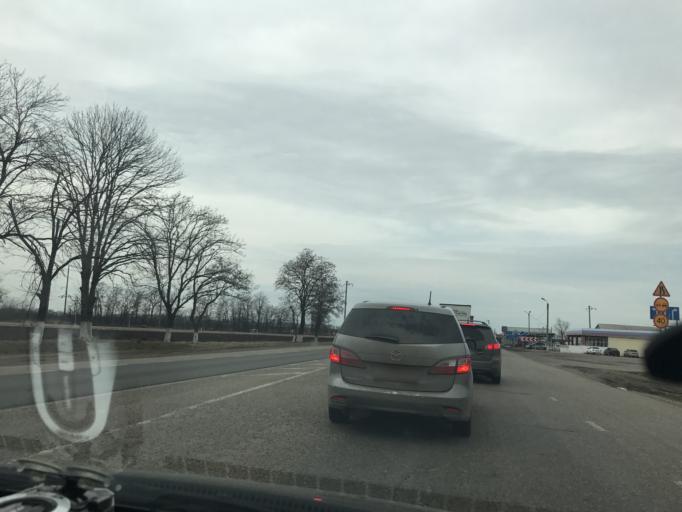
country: RU
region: Krasnodarskiy
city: Zavetnyy
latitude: 44.9228
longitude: 41.1327
